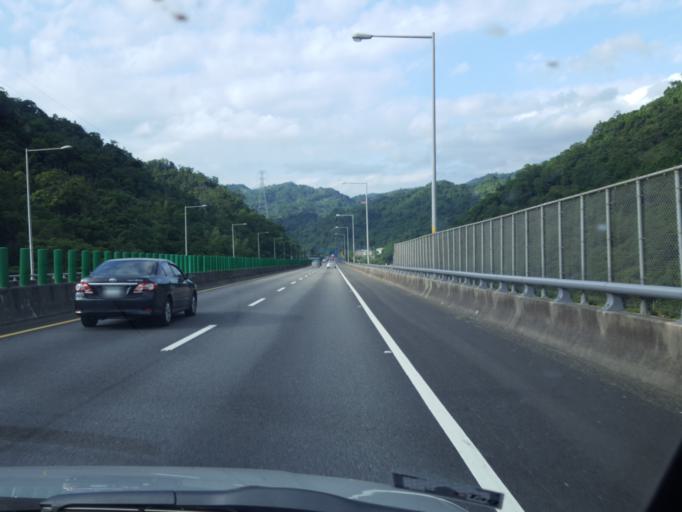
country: TW
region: Taipei
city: Taipei
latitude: 24.9983
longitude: 121.6518
